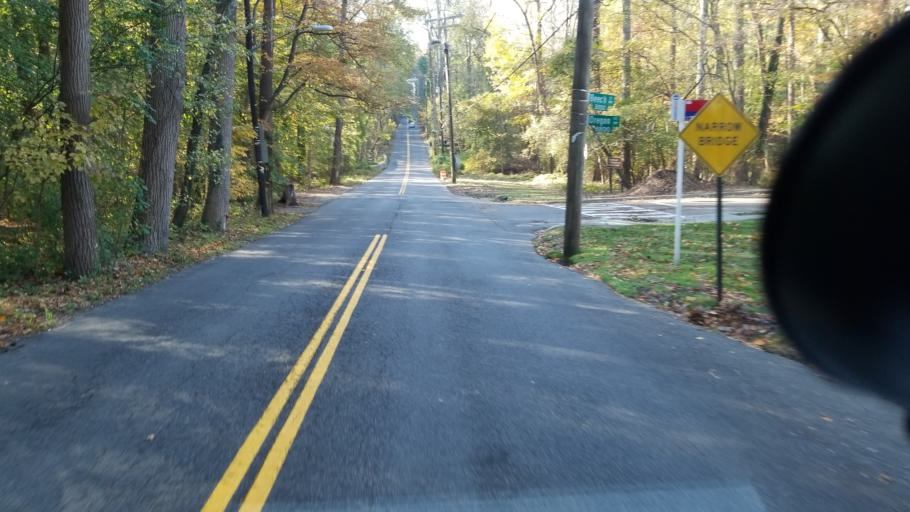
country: US
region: Maryland
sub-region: Montgomery County
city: Chevy Chase
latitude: 38.9774
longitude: -77.0525
